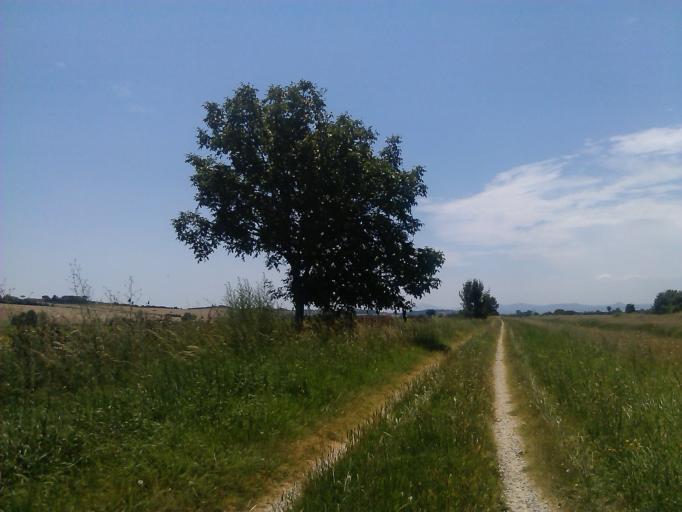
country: IT
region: Tuscany
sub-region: Province of Arezzo
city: Cesa
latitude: 43.2929
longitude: 11.8417
